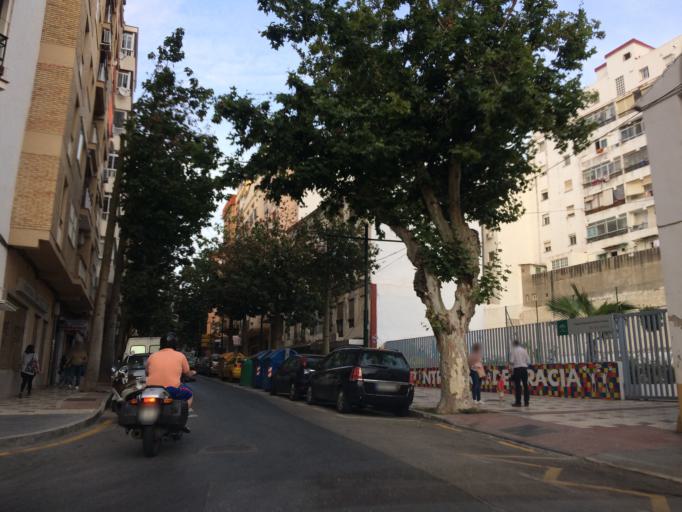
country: ES
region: Andalusia
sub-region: Provincia de Malaga
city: Malaga
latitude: 36.7270
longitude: -4.4135
